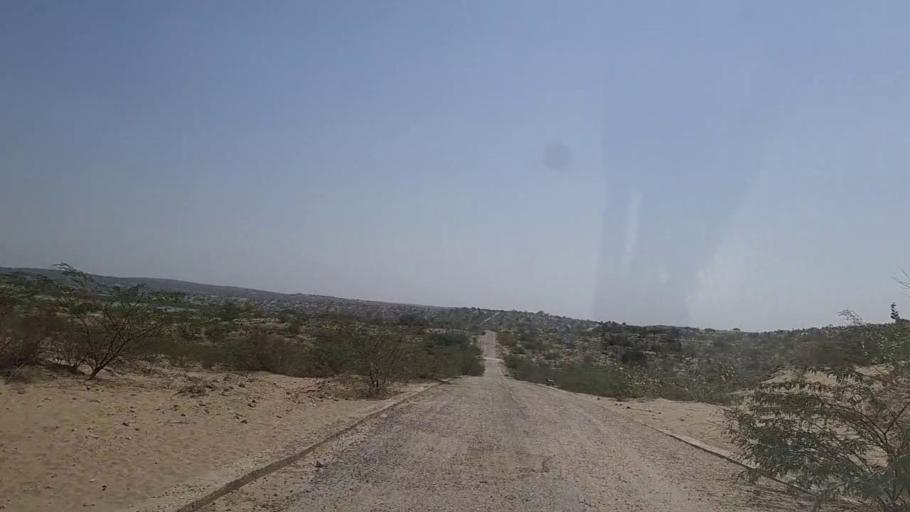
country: PK
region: Sindh
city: Diplo
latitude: 24.5207
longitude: 69.3596
